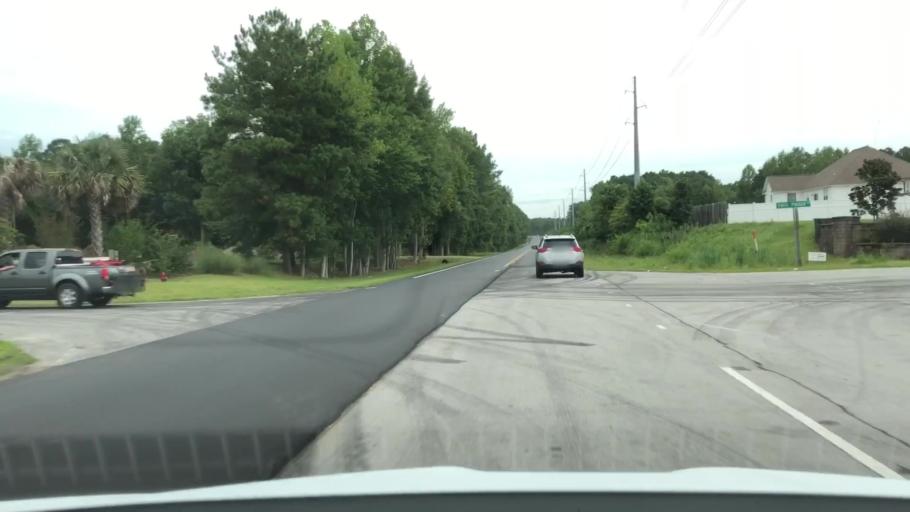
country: US
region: North Carolina
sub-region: Carteret County
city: Cape Carteret
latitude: 34.7616
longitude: -77.0951
